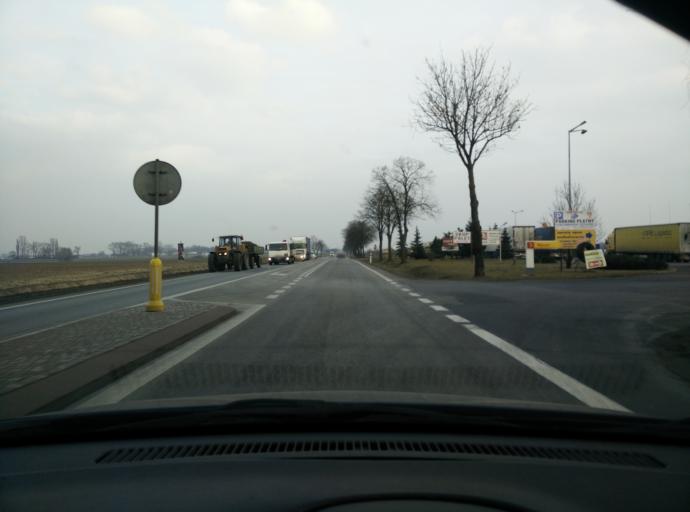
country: PL
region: Greater Poland Voivodeship
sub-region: Powiat sredzki
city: Zaniemysl
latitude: 52.2344
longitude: 17.1761
